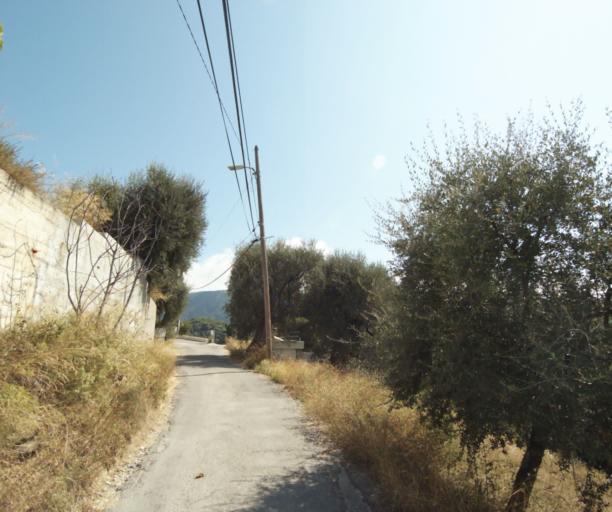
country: FR
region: Provence-Alpes-Cote d'Azur
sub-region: Departement des Alpes-Maritimes
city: Drap
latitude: 43.7570
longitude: 7.3293
